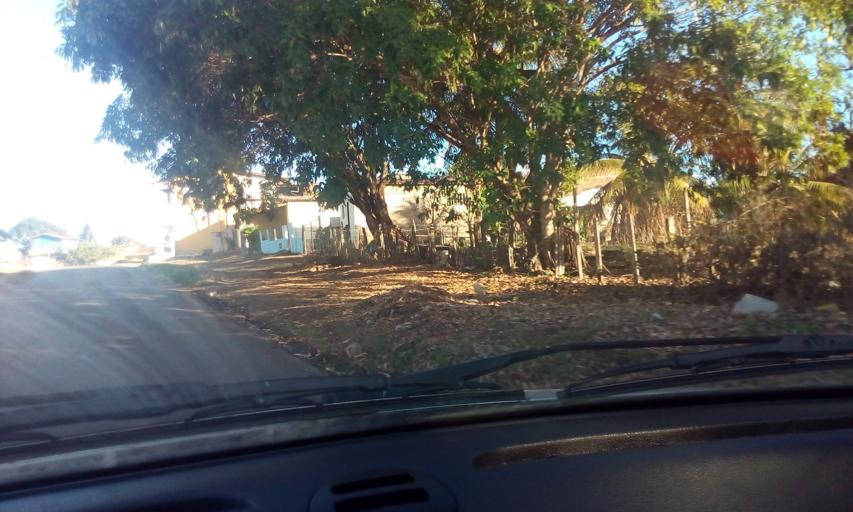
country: BR
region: Rio Grande do Norte
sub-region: Parnamirim
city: Parnamirim
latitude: -5.9587
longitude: -35.1659
